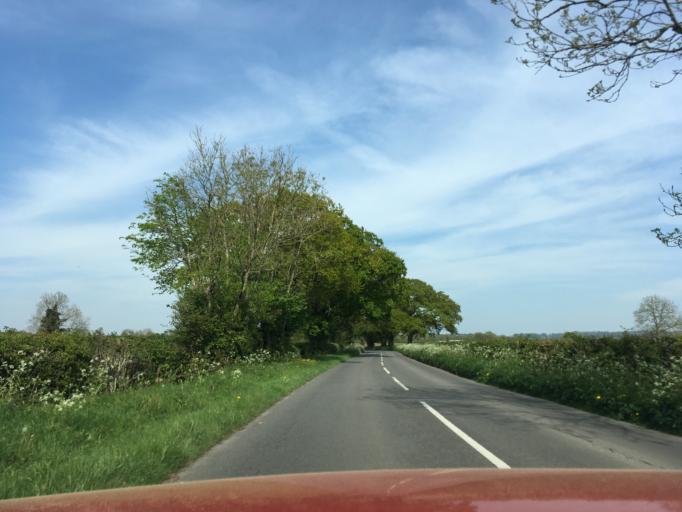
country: GB
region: England
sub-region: South Gloucestershire
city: Chipping Sodbury
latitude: 51.5178
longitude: -2.4020
